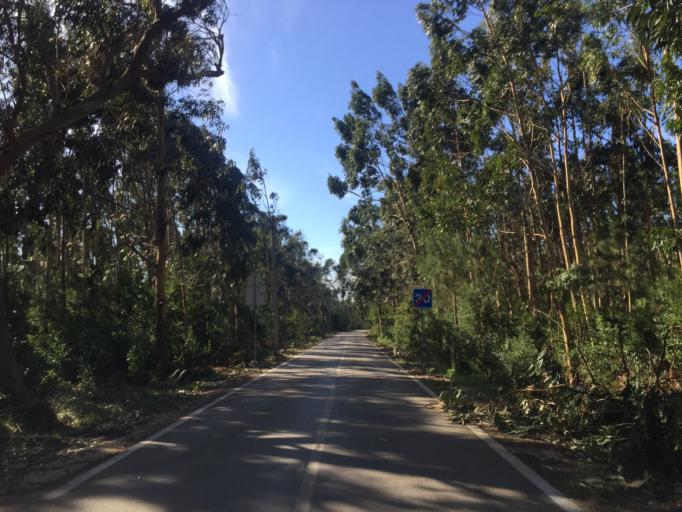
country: PT
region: Coimbra
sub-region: Figueira da Foz
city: Buarcos
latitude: 40.1908
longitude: -8.8863
